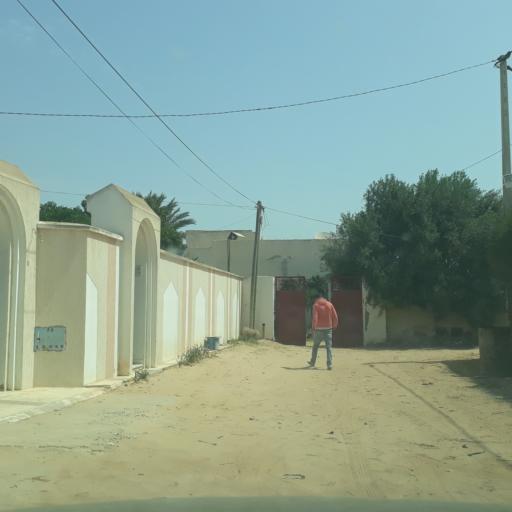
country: TN
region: Safaqis
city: Al Qarmadah
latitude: 34.7958
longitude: 10.7636
